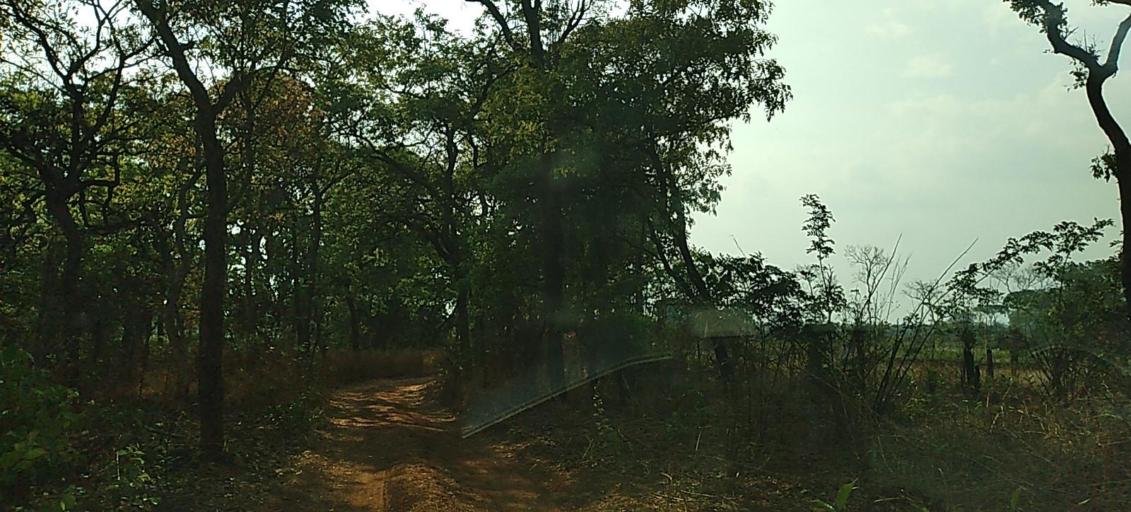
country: ZM
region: North-Western
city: Solwezi
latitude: -12.0581
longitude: 26.1617
